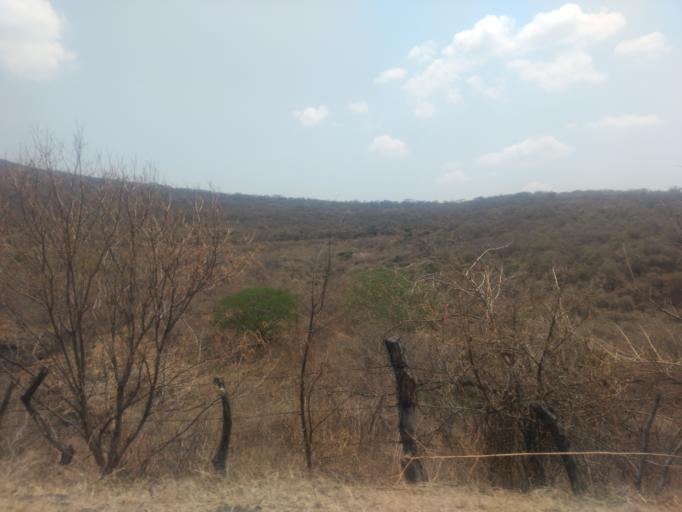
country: MX
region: Morelos
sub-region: Mazatepec
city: Cuauchichinola
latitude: 18.6505
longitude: -99.3989
